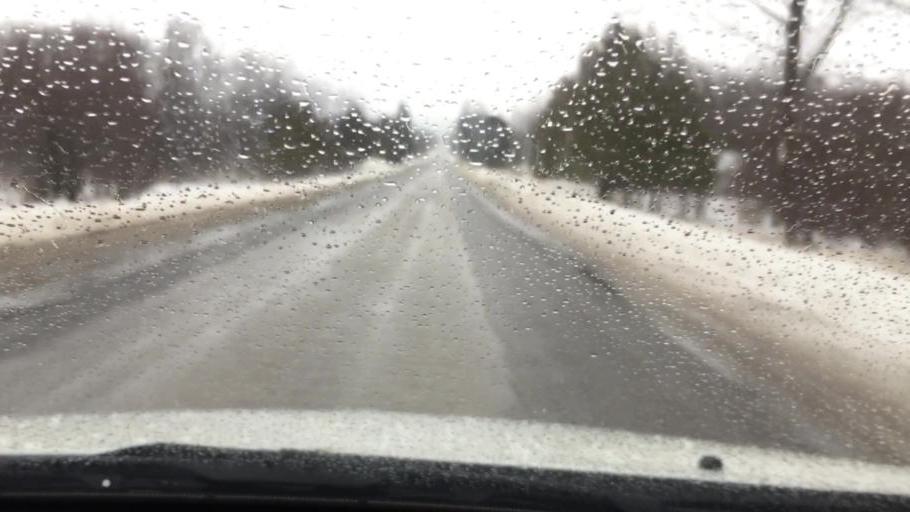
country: US
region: Michigan
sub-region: Charlevoix County
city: East Jordan
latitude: 45.1325
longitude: -85.1483
